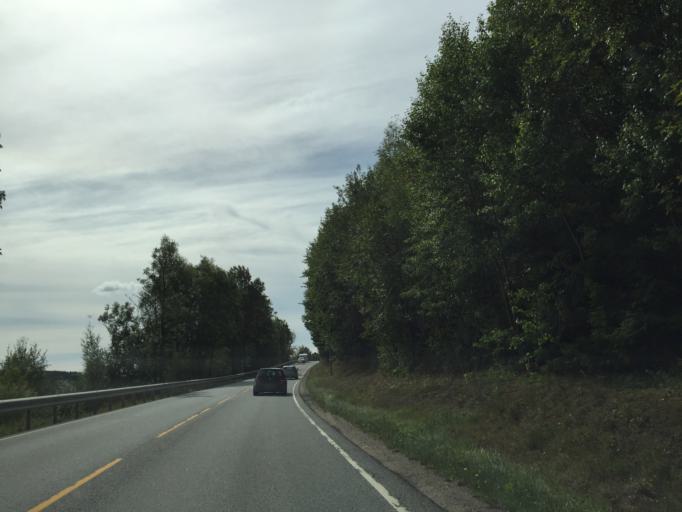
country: NO
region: Ostfold
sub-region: Fredrikstad
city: Fredrikstad
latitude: 59.2811
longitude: 10.9017
